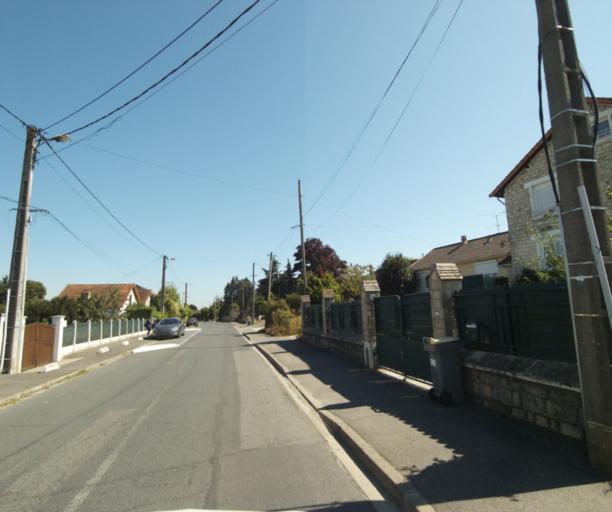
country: FR
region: Ile-de-France
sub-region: Departement de l'Essonne
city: Itteville
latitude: 48.5192
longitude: 2.3480
